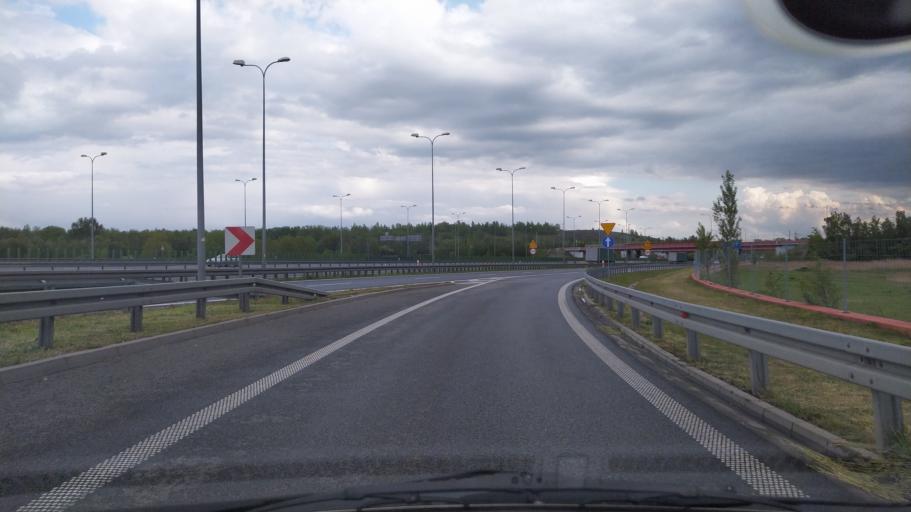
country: PL
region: Silesian Voivodeship
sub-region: Powiat gliwicki
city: Przyszowice
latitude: 50.2774
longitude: 18.7270
